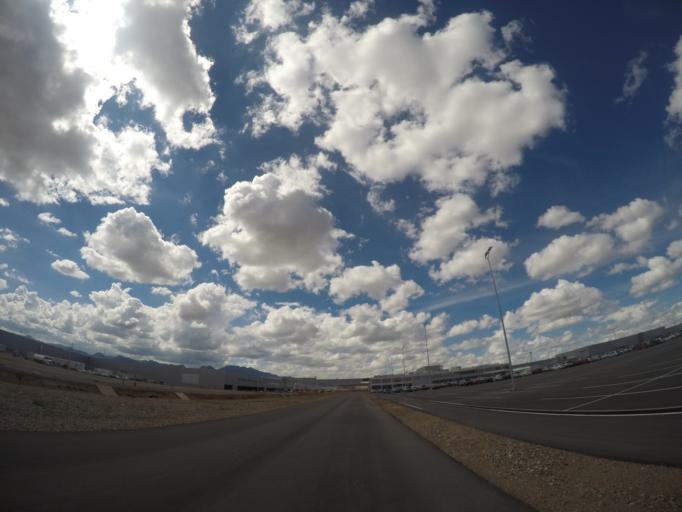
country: MX
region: San Luis Potosi
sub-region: Zaragoza
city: Cerro Gordo
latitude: 21.9659
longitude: -100.8469
